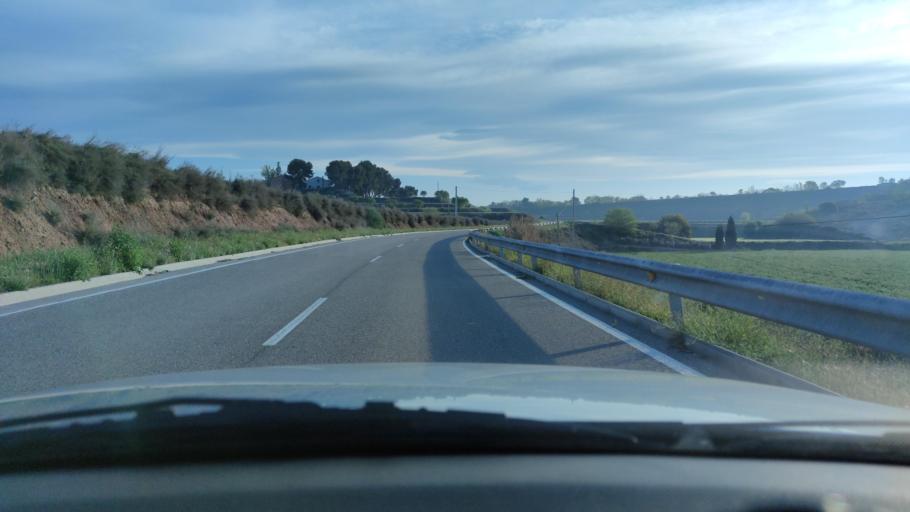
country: ES
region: Catalonia
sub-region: Provincia de Lleida
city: Castellsera
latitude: 41.7607
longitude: 0.9977
